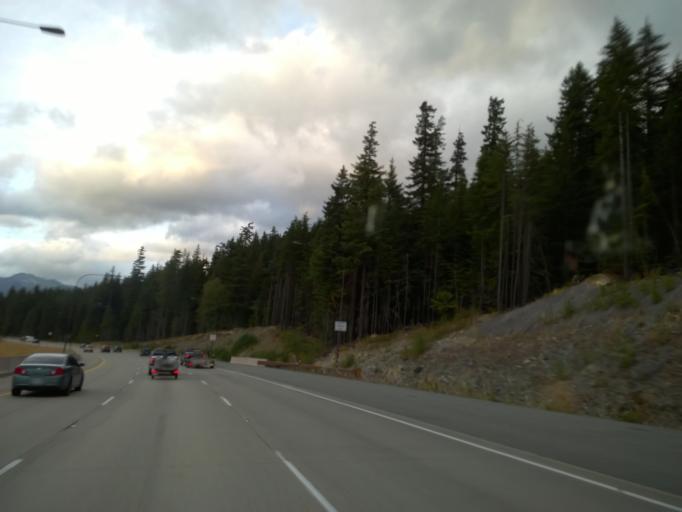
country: US
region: Washington
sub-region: King County
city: Tanner
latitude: 47.3669
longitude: -121.3723
